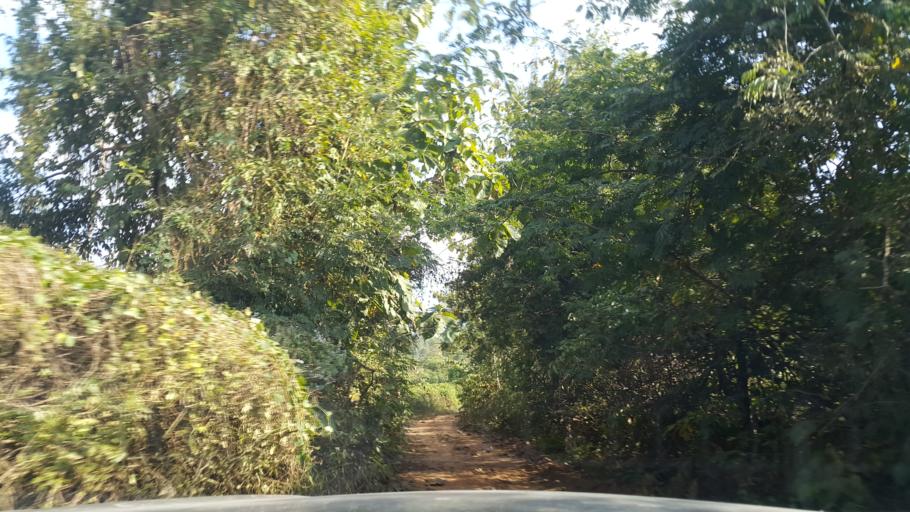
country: TH
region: Lamphun
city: Mae Tha
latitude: 18.5292
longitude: 99.1078
